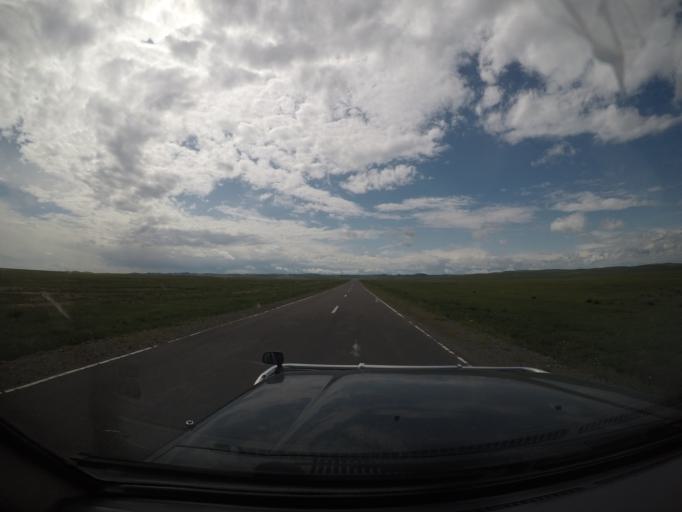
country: MN
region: Hentiy
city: Moron
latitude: 47.4181
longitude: 109.9262
